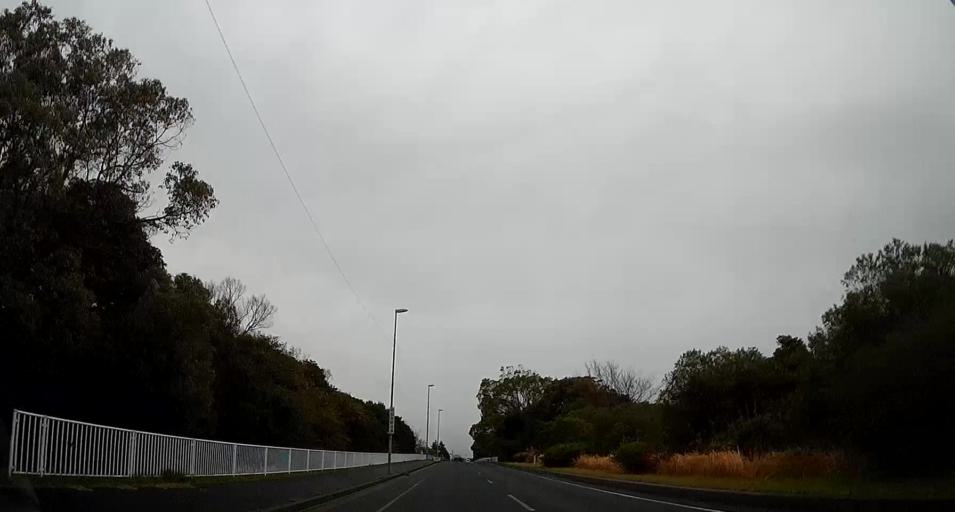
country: JP
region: Chiba
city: Chiba
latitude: 35.6516
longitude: 140.0598
